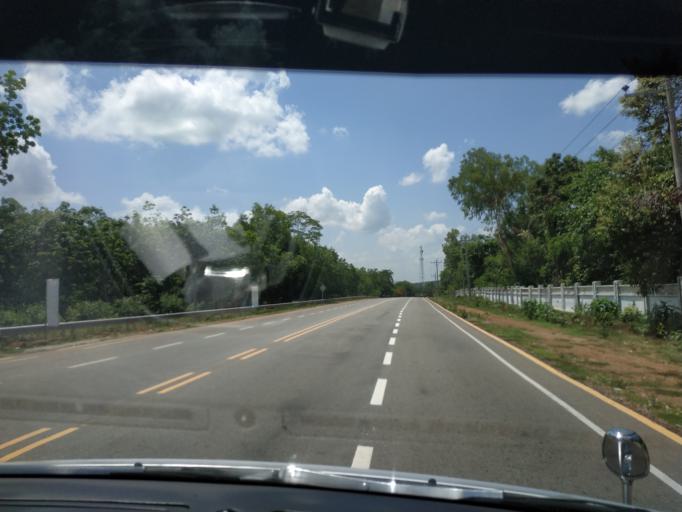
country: MM
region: Mon
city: Kyaikto
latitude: 17.3404
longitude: 97.0380
